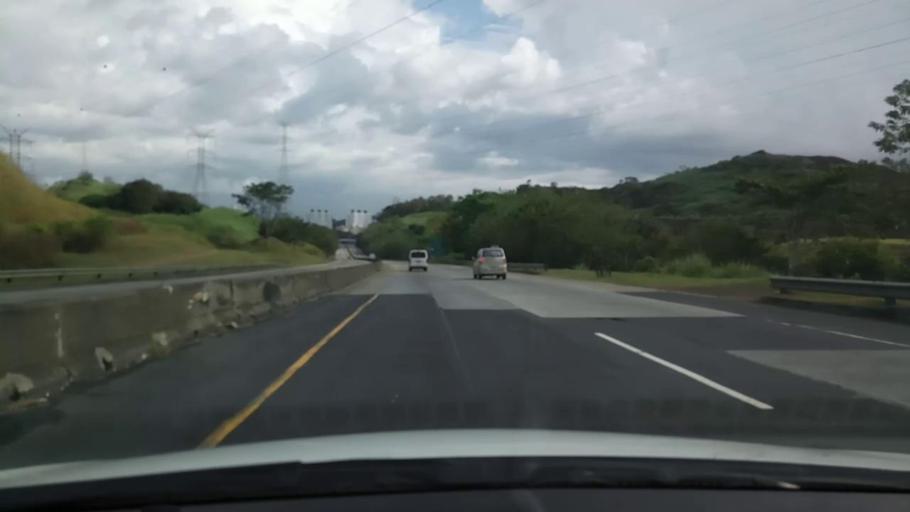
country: PA
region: Panama
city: Las Cumbres
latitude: 9.0458
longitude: -79.5419
